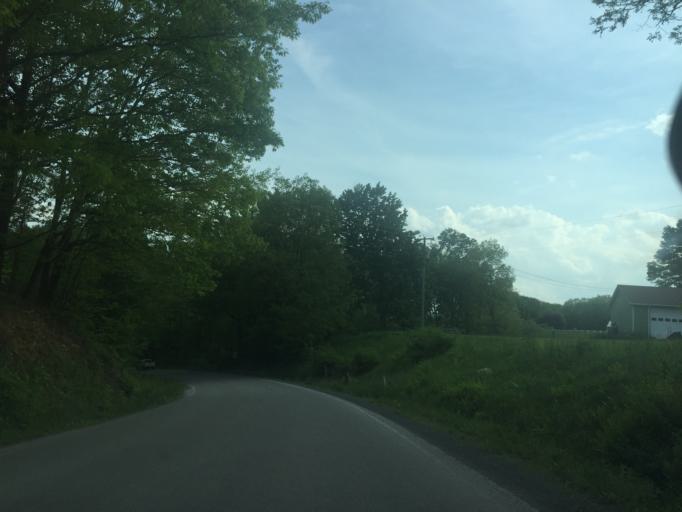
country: US
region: West Virginia
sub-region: Tucker County
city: Parsons
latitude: 38.9890
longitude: -79.4736
